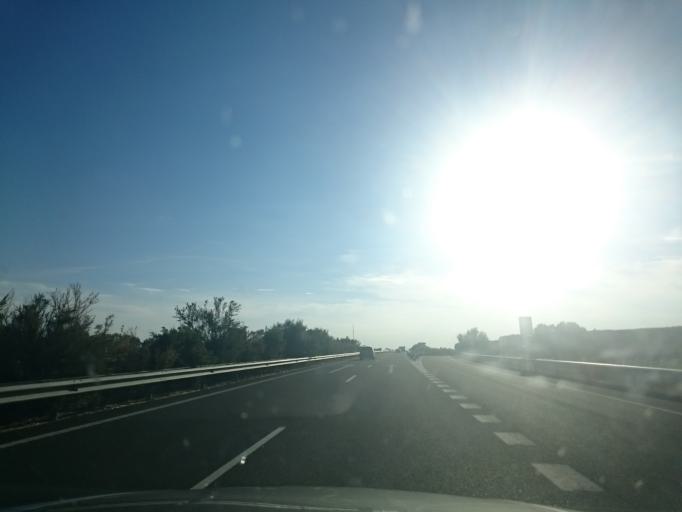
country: ES
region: Castille and Leon
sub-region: Provincia de Palencia
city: Carrion de los Condes
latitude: 42.3497
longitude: -4.6191
